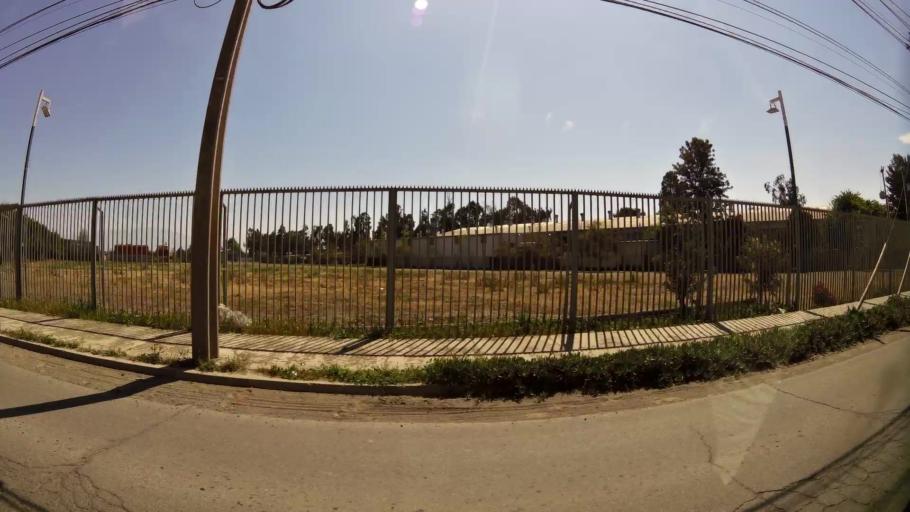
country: CL
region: Santiago Metropolitan
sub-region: Provincia de Santiago
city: Lo Prado
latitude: -33.3853
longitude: -70.7516
